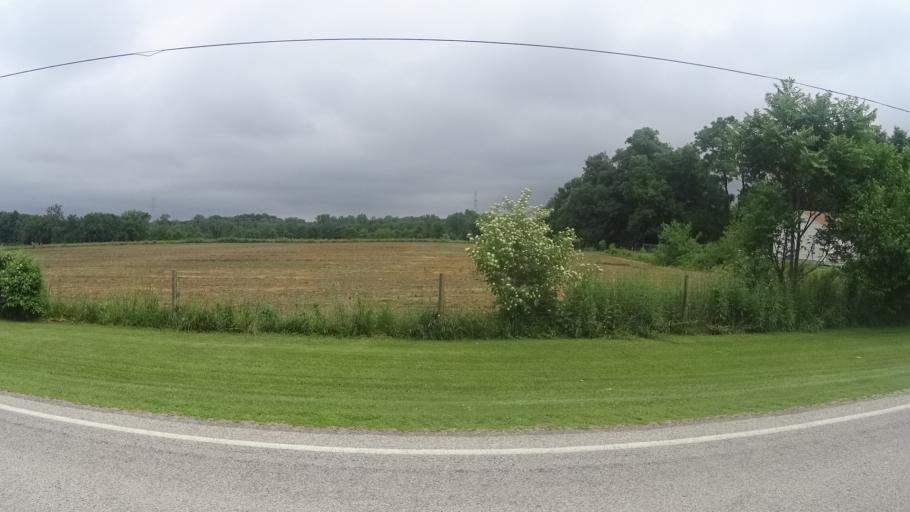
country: US
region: Ohio
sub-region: Erie County
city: Huron
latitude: 41.3307
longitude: -82.5089
